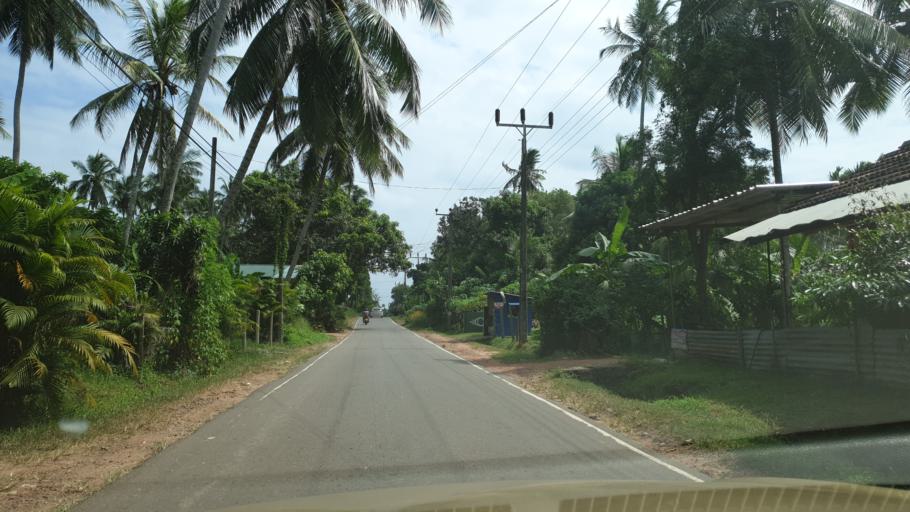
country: LK
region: North Western
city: Kuliyapitiya
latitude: 7.3477
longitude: 79.9809
